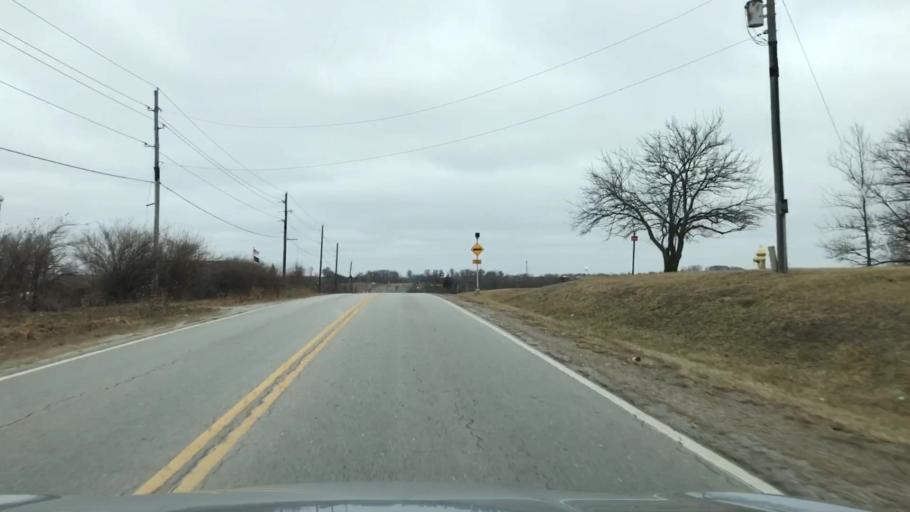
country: US
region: Missouri
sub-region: Clay County
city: Liberty
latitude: 39.2743
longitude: -94.4167
